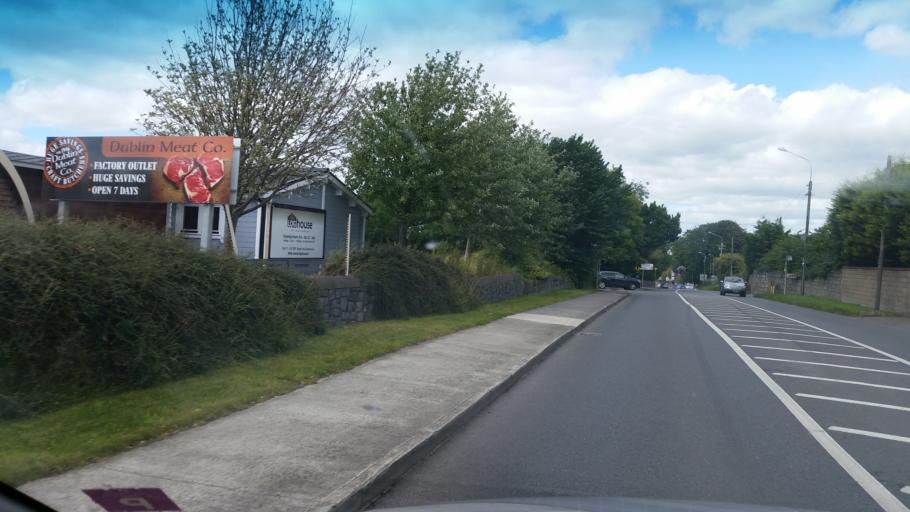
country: IE
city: Darndale
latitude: 53.4232
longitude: -6.1763
